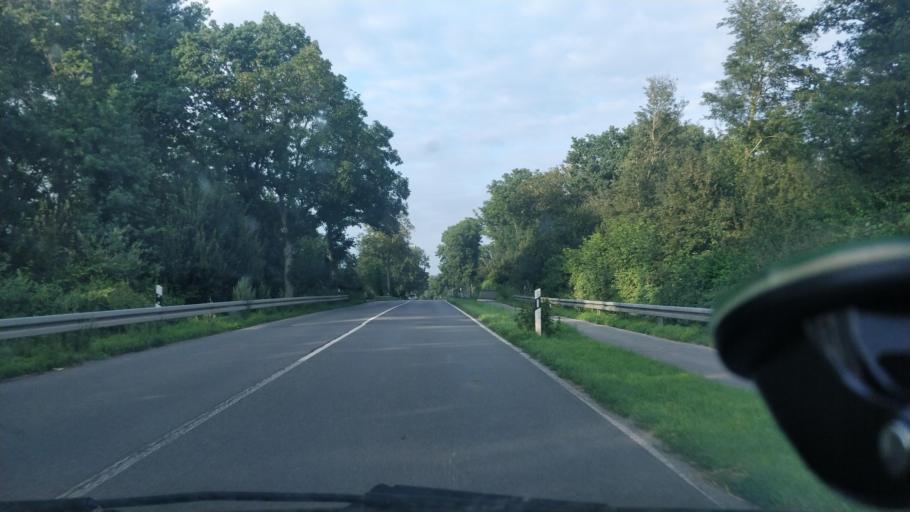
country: DE
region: North Rhine-Westphalia
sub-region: Regierungsbezirk Dusseldorf
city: Rheurdt
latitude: 51.4866
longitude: 6.4961
